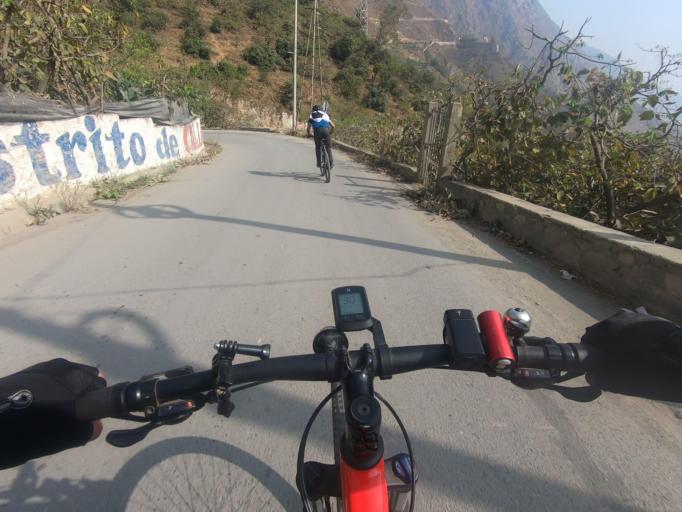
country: PE
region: Lima
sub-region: Provincia de Huarochiri
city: Callahuanca
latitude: -11.8284
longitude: -76.6158
